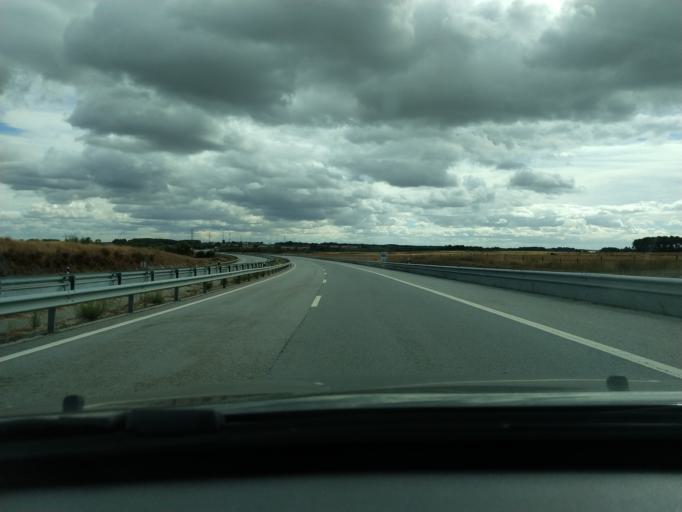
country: PT
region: Guarda
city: Alcains
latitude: 40.0142
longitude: -7.4668
